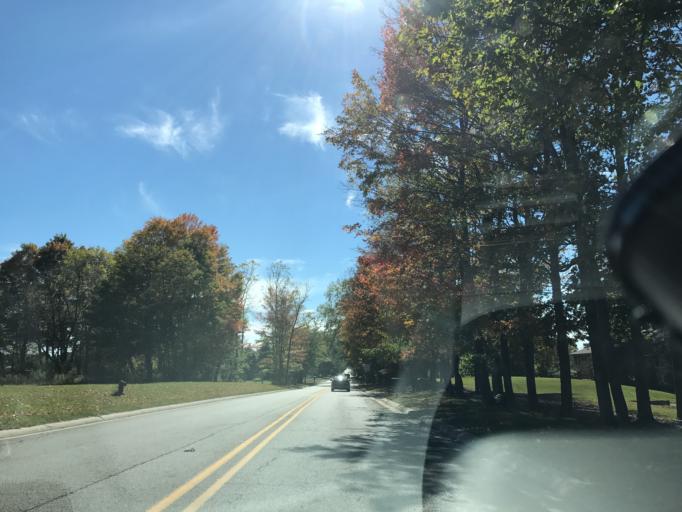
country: US
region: Michigan
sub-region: Oakland County
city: South Lyon
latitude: 42.4604
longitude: -83.6317
